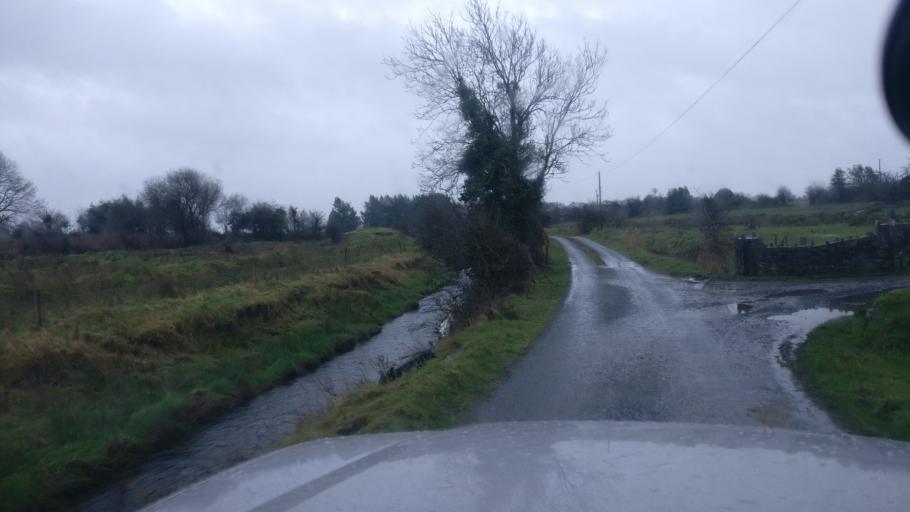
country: IE
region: Connaught
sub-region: County Galway
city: Ballinasloe
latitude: 53.2465
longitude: -8.3464
